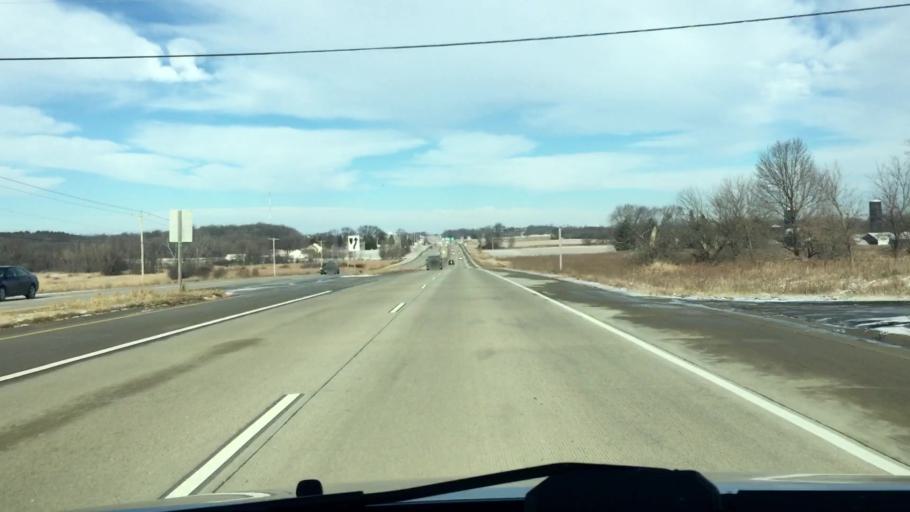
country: US
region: Wisconsin
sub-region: Waukesha County
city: Mukwonago
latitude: 42.9111
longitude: -88.3454
